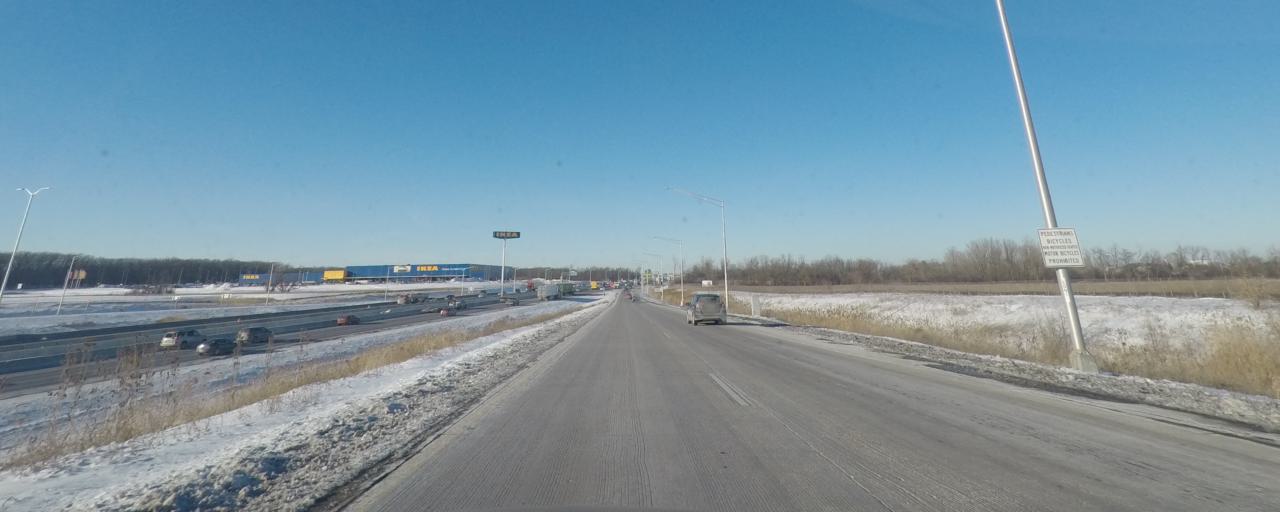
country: US
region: Wisconsin
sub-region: Milwaukee County
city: Greendale
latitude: 42.9022
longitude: -87.9353
